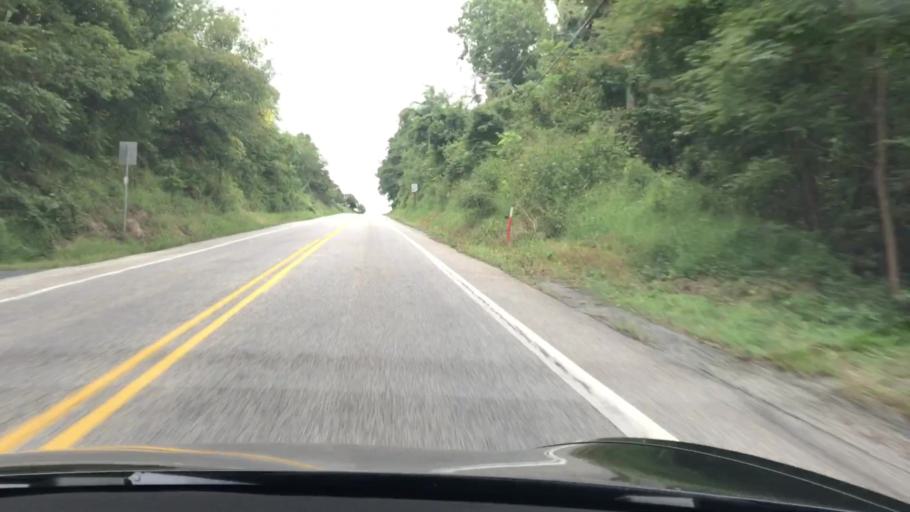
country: US
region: Pennsylvania
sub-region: Cumberland County
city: Shiremanstown
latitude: 40.1578
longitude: -76.9703
